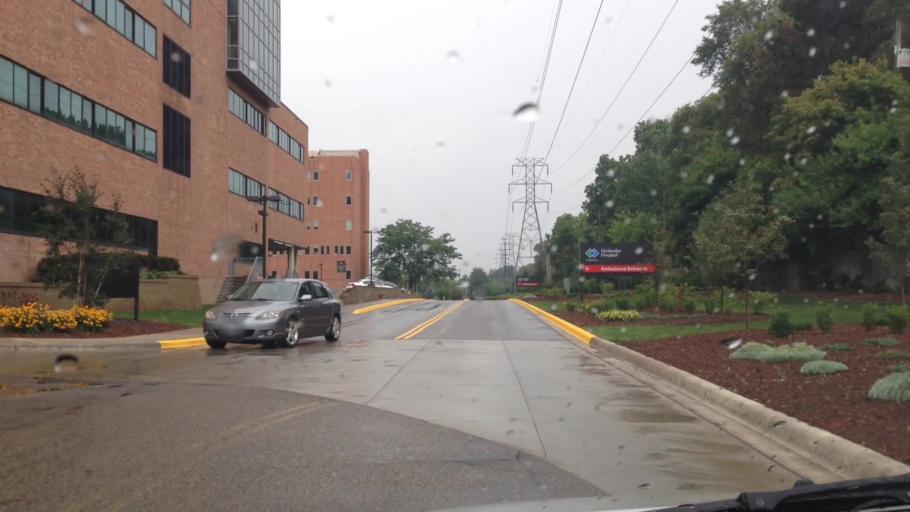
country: US
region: Minnesota
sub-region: Hennepin County
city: Saint Louis Park
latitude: 44.9290
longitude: -93.3611
